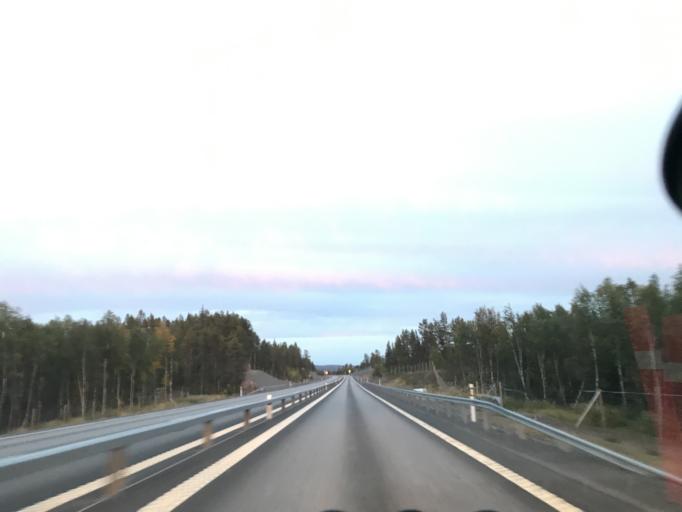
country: SE
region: Norrbotten
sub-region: Gallivare Kommun
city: Malmberget
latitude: 67.6799
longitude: 20.8792
